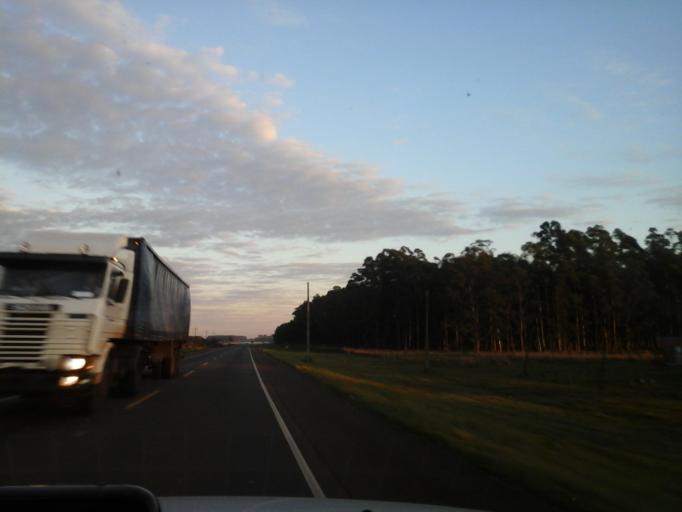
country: PY
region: Itapua
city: General Delgado
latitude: -27.0722
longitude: -56.6046
